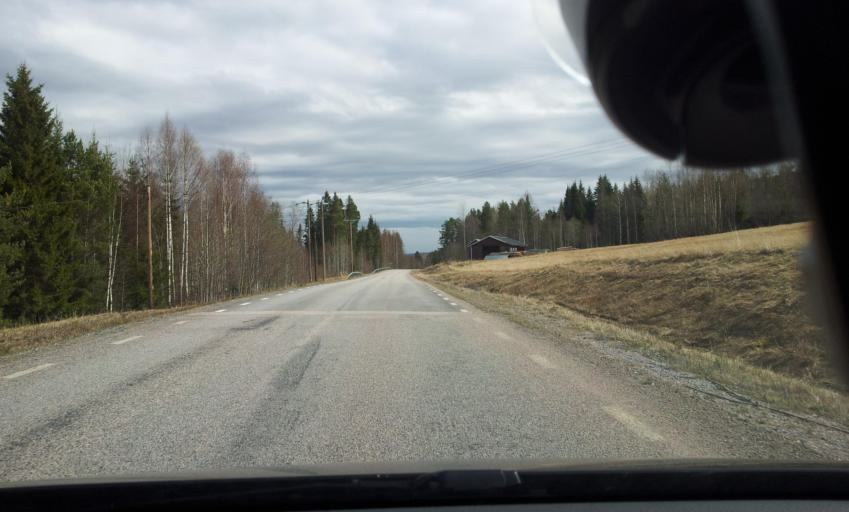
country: SE
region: Gaevleborg
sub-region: Ljusdals Kommun
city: Ljusdal
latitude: 61.7689
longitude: 16.0193
